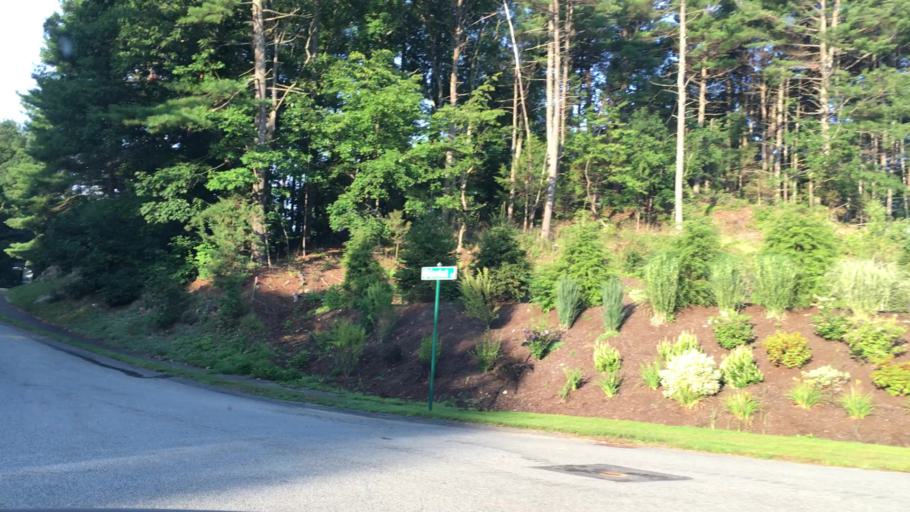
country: US
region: Massachusetts
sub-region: Norfolk County
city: Wellesley
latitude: 42.3224
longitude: -71.2935
